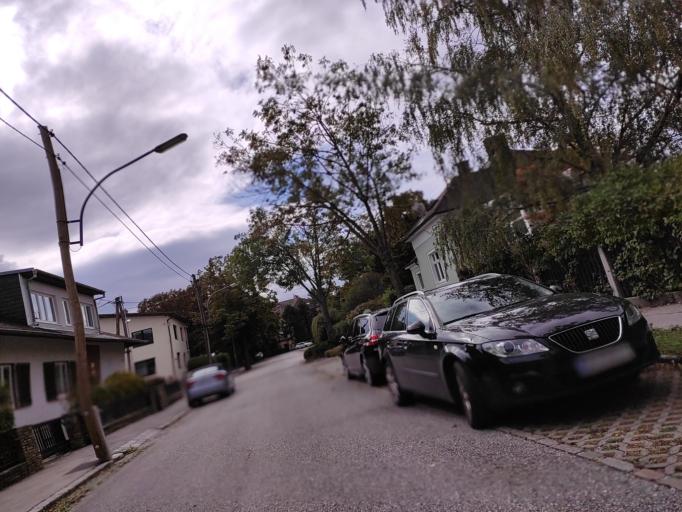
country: AT
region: Lower Austria
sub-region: Politischer Bezirk Baden
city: Baden
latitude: 48.0042
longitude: 16.2472
